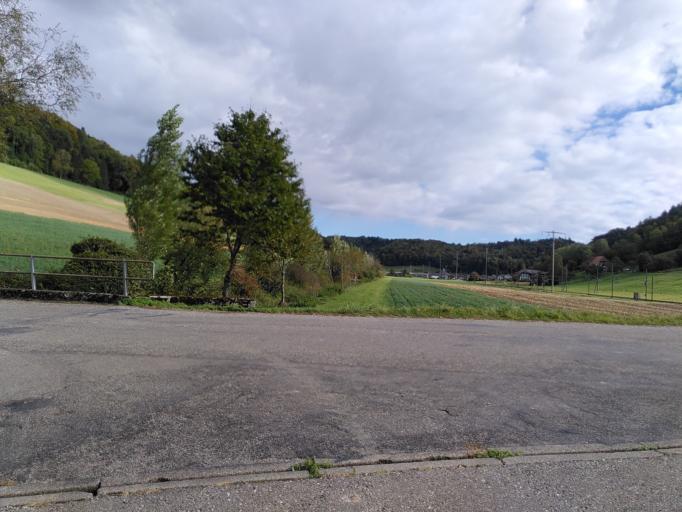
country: CH
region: Bern
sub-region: Oberaargau
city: Seeberg
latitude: 47.1347
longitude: 7.6836
